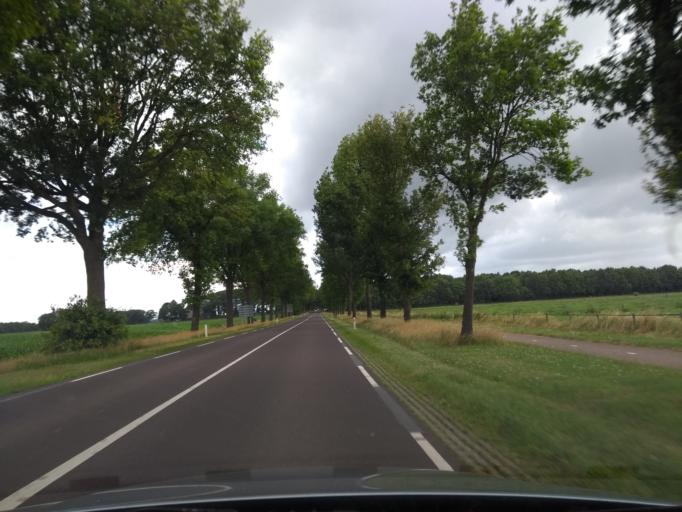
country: NL
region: Overijssel
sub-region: Gemeente Twenterand
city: Vroomshoop
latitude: 52.4092
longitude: 6.5568
